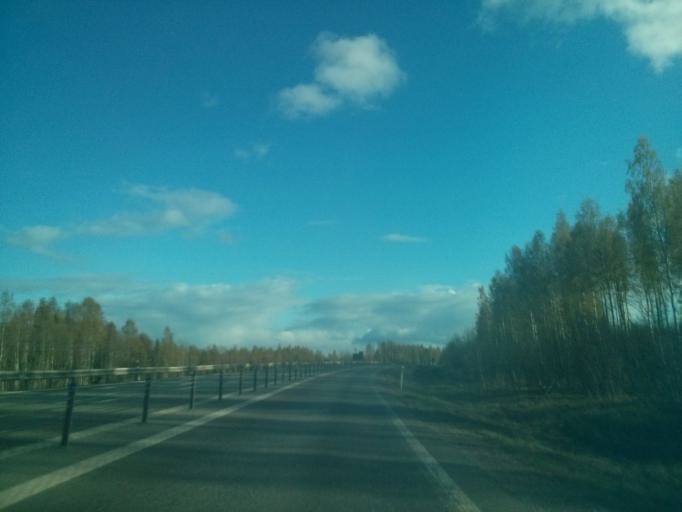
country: SE
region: Vaesternorrland
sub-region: Sundsvalls Kommun
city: Njurundabommen
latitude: 62.1632
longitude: 17.3555
